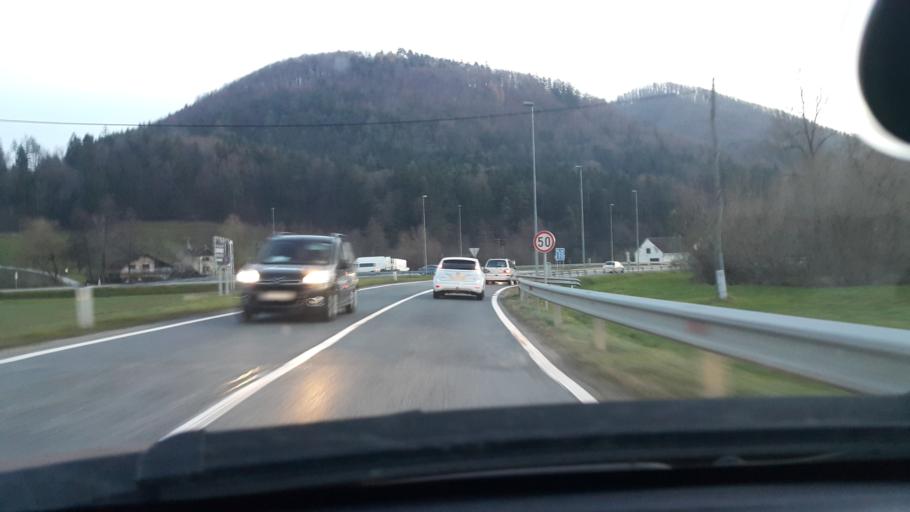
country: SI
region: Dobrna
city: Dobrna
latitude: 46.3242
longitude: 15.1841
